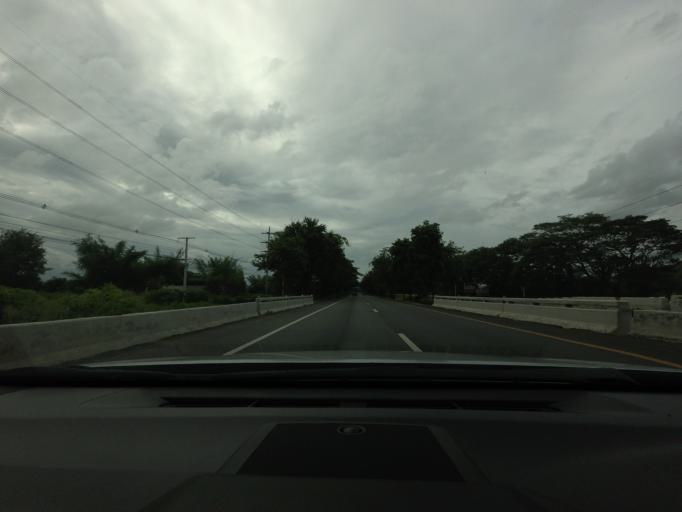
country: TH
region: Prachuap Khiri Khan
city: Hua Hin
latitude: 12.6005
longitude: 99.8624
